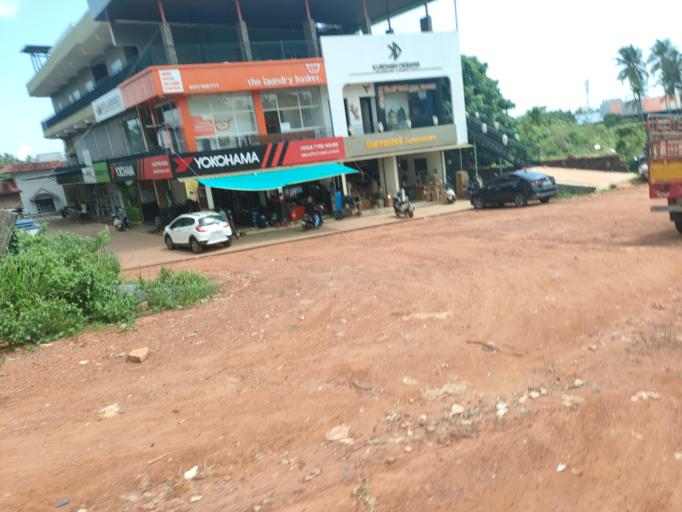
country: IN
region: Kerala
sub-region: Kasaragod District
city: Kasaragod
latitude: 12.5138
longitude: 75.0018
